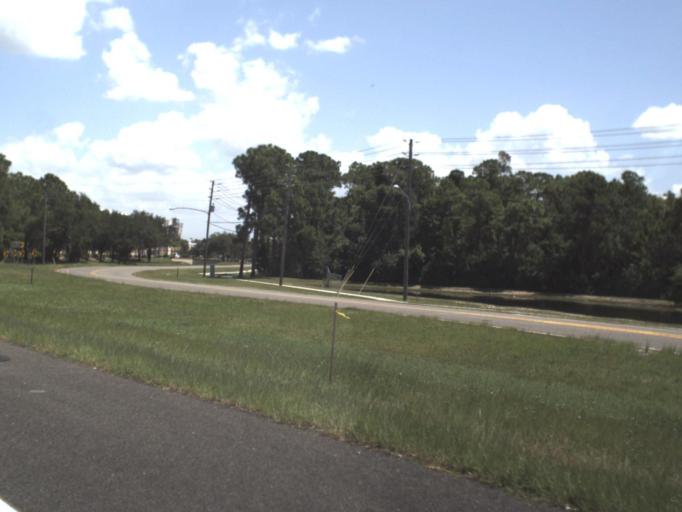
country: US
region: Florida
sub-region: Pinellas County
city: Gandy
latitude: 27.8572
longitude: -82.6531
